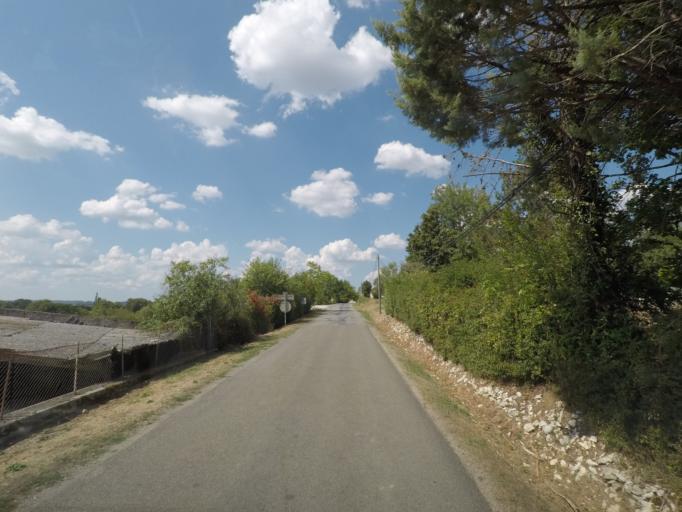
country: FR
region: Midi-Pyrenees
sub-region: Departement du Lot
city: Le Vigan
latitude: 44.5939
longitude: 1.5823
